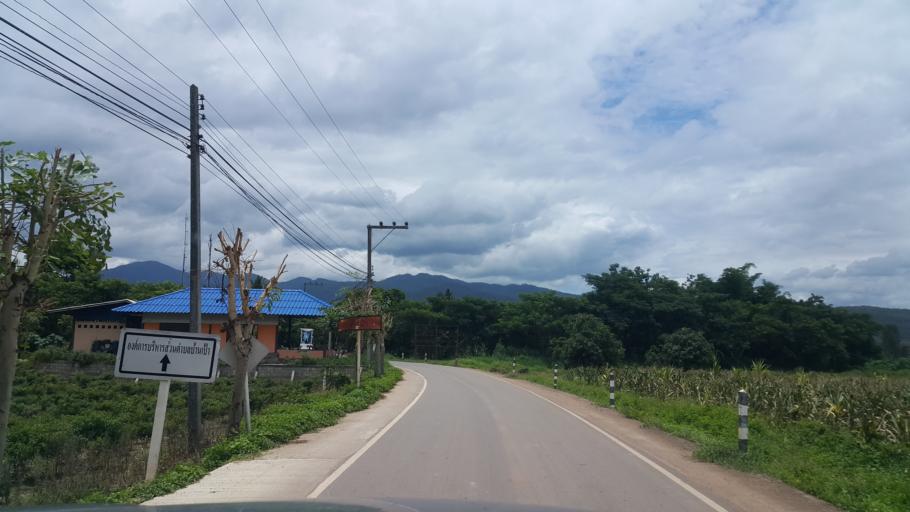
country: TH
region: Chiang Mai
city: Mae Taeng
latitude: 19.1870
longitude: 98.9934
